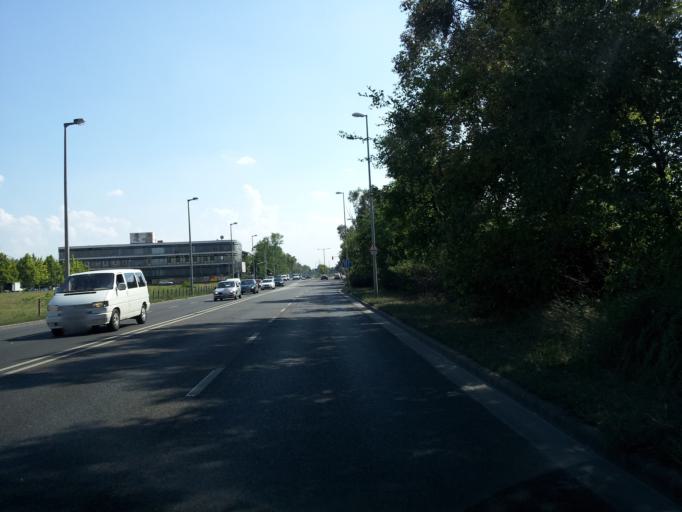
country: HU
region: Budapest
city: Budapest XI. keruelet
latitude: 47.4590
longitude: 19.0474
